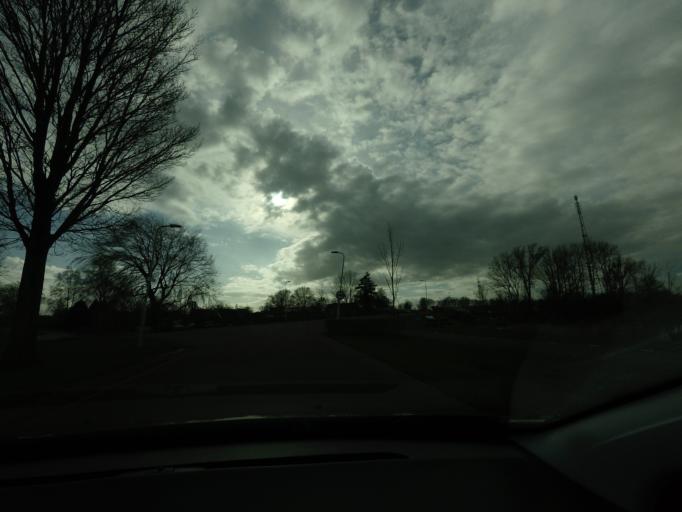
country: NL
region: Friesland
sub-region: Gemeente Boarnsterhim
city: Jirnsum
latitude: 53.0838
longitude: 5.7976
